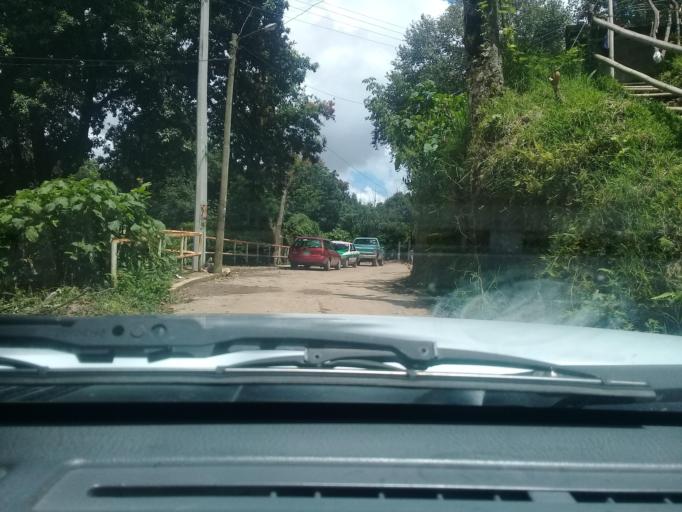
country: MX
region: Veracruz
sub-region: Tlalnelhuayocan
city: Otilpan
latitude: 19.5369
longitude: -96.9720
